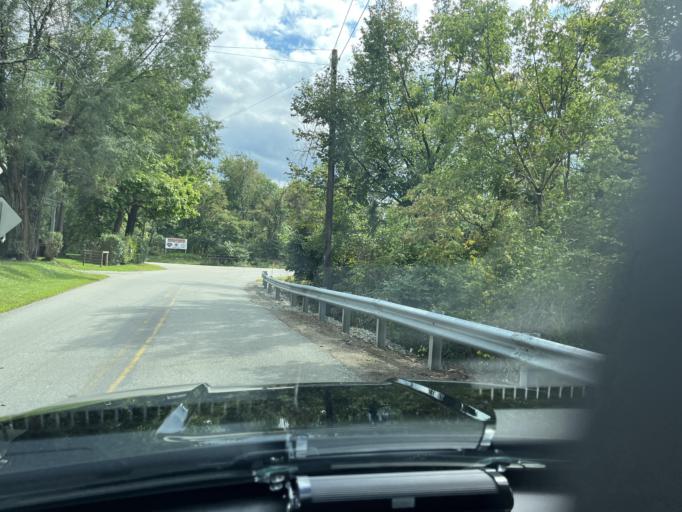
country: US
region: Pennsylvania
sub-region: Fayette County
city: Leith-Hatfield
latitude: 39.8822
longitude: -79.7167
